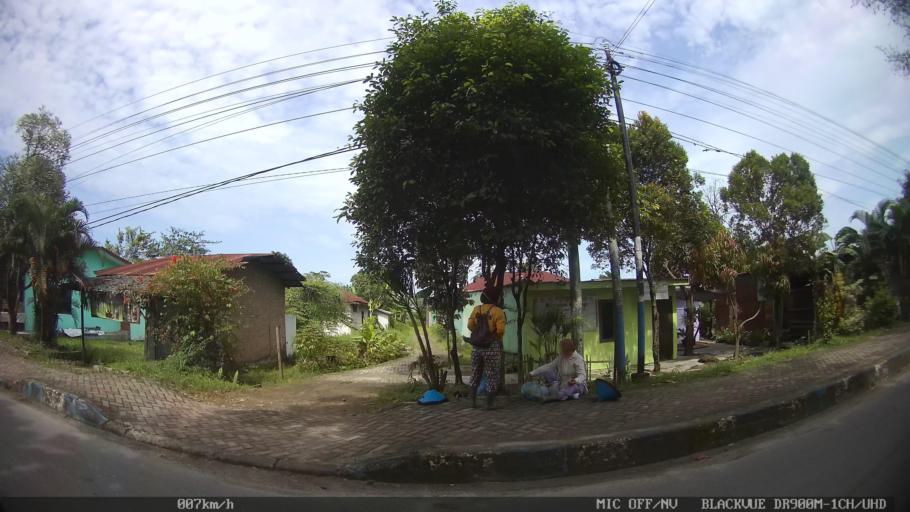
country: ID
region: North Sumatra
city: Percut
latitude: 3.5968
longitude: 98.8073
